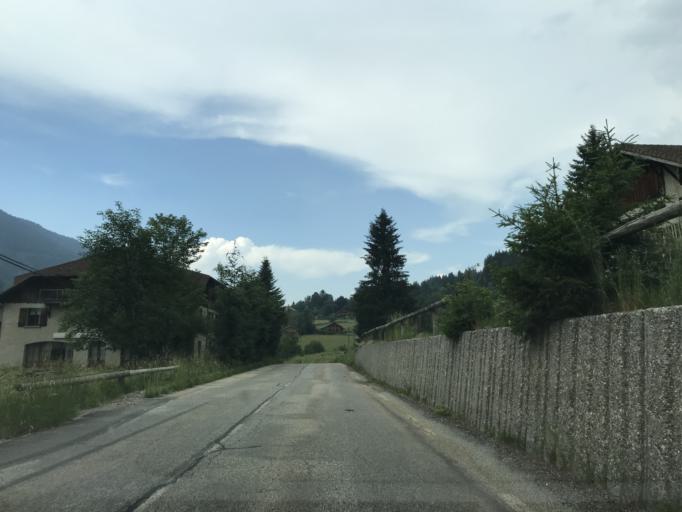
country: FR
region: Rhone-Alpes
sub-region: Departement de l'Isere
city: Theys
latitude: 45.3016
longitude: 6.0812
